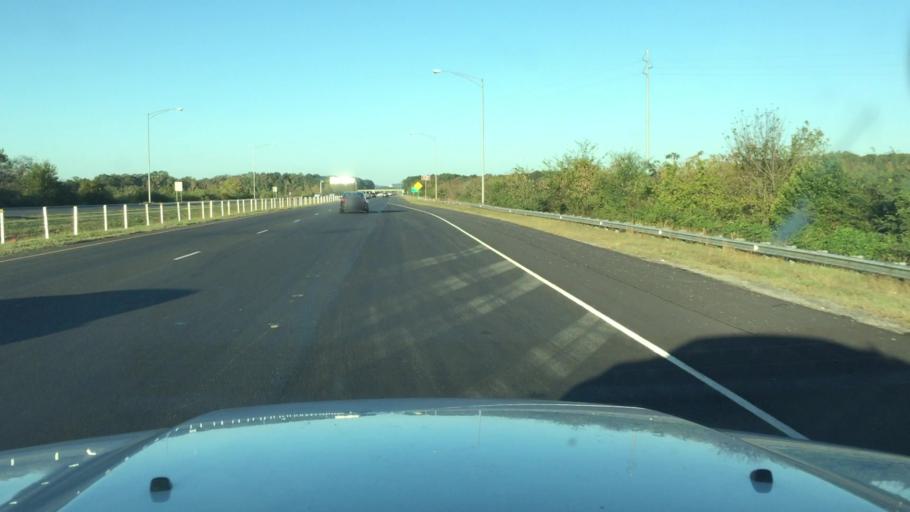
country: US
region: Alabama
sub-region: Etowah County
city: Gadsden
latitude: 33.9918
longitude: -86.0113
